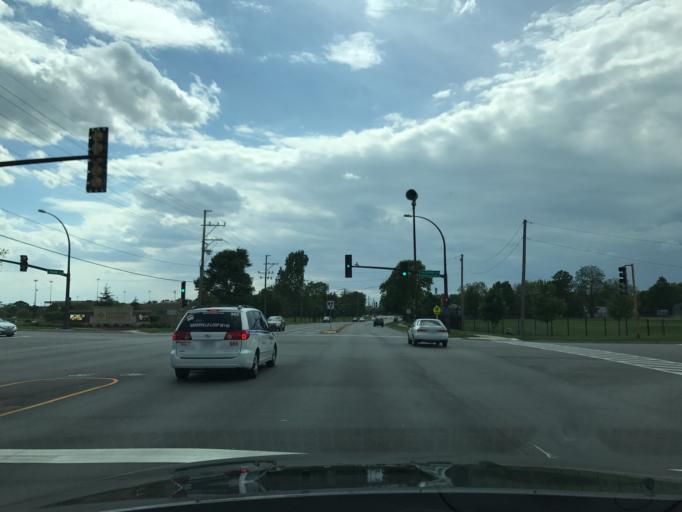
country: US
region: Illinois
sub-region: DuPage County
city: Lisle
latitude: 41.7823
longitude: -88.0922
